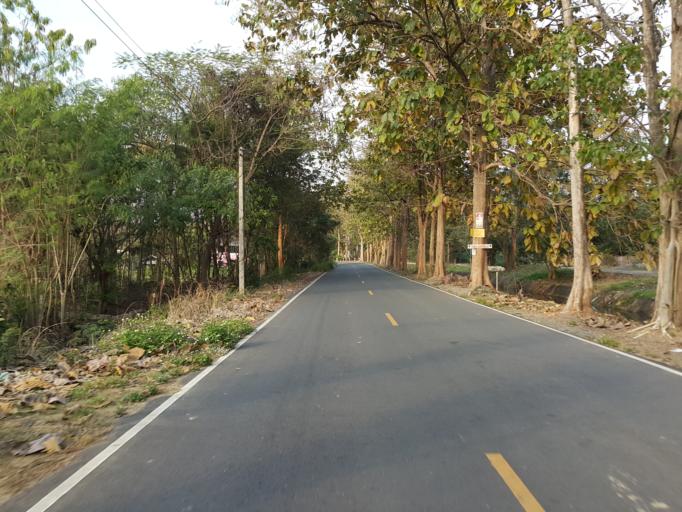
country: TH
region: Chiang Mai
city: San Sai
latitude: 18.8885
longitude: 99.1413
